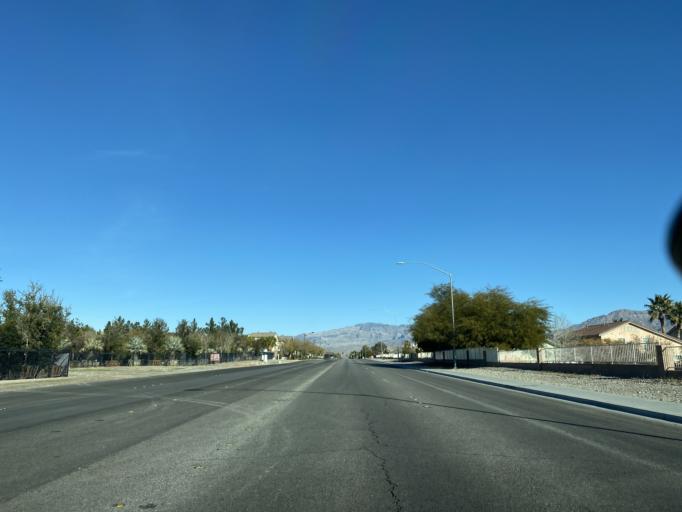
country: US
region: Nevada
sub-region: Clark County
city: Summerlin South
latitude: 36.2939
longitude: -115.2787
